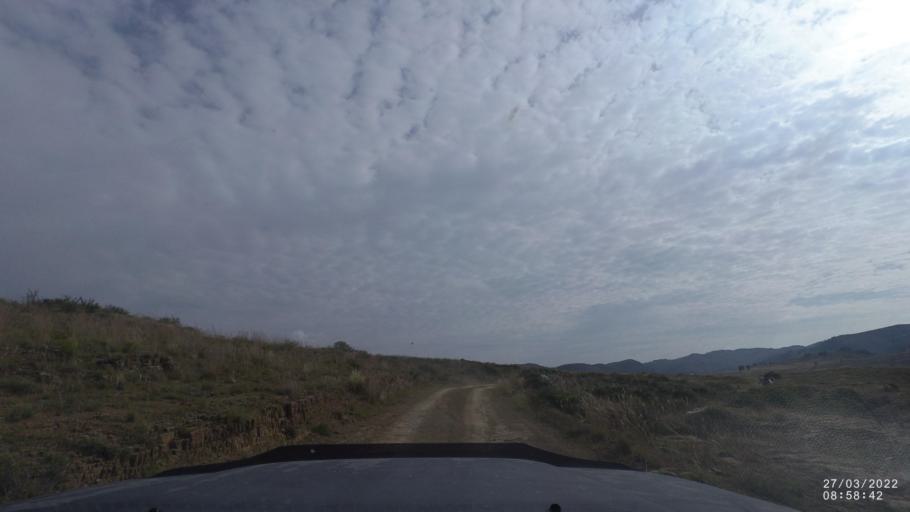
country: BO
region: Cochabamba
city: Cliza
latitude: -17.7416
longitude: -65.8564
